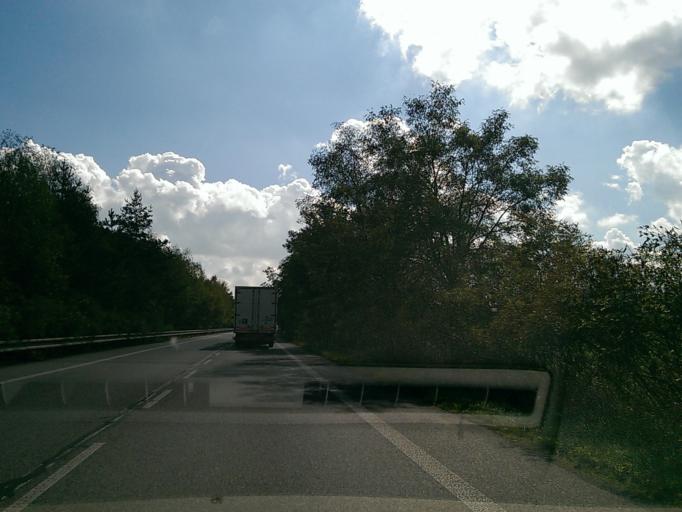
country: CZ
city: Doksy
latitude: 50.5769
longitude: 14.6382
